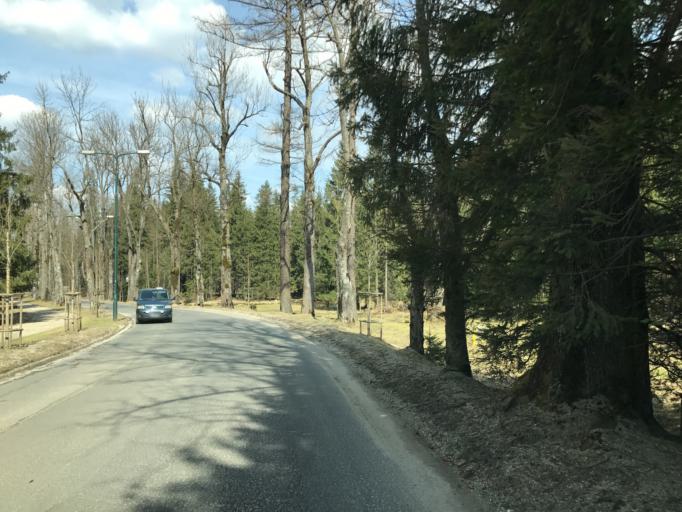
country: PL
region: Lesser Poland Voivodeship
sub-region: Powiat tatrzanski
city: Zakopane
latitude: 49.2774
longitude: 19.9809
